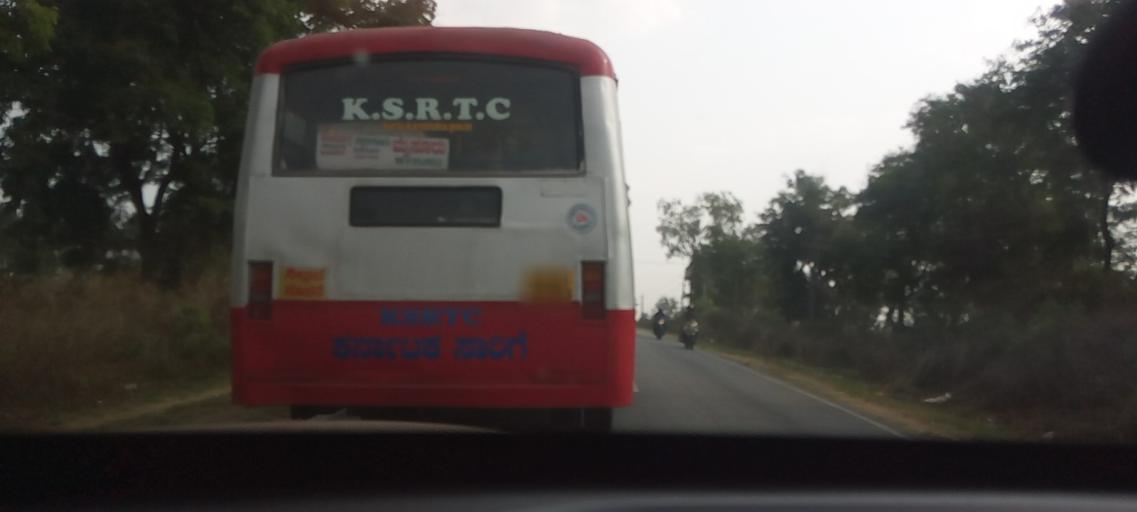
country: IN
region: Karnataka
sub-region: Hassan
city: Hassan
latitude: 13.0230
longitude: 76.0687
